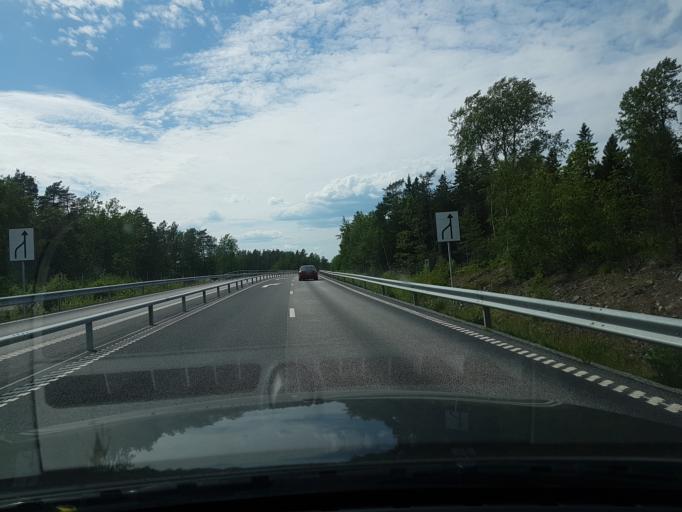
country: SE
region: Stockholm
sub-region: Norrtalje Kommun
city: Bjorko
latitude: 59.7195
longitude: 18.9345
